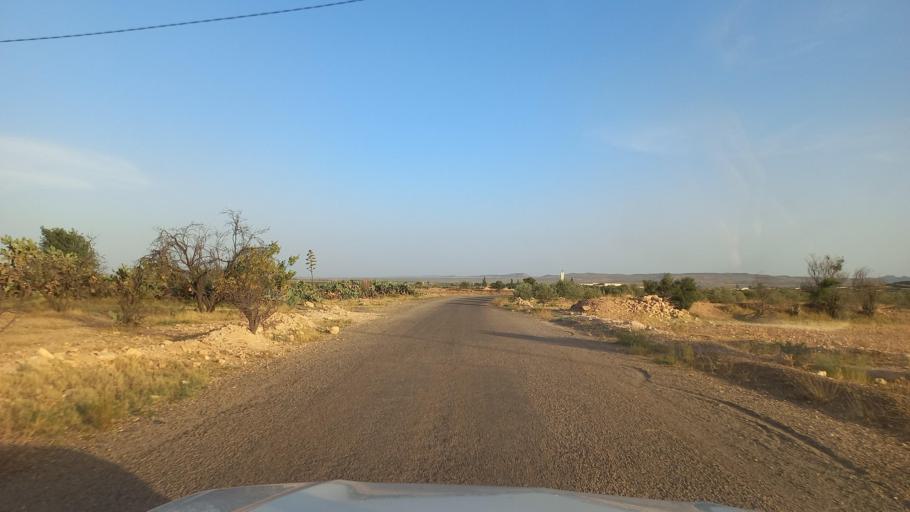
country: TN
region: Al Qasrayn
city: Kasserine
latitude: 35.2692
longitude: 8.9308
